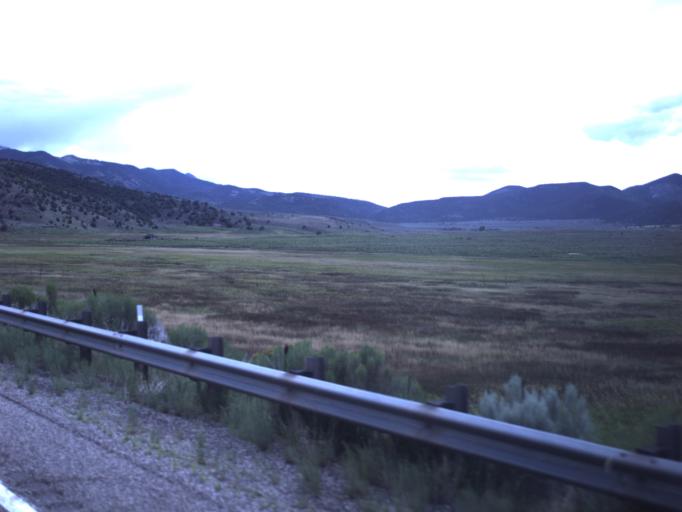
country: US
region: Utah
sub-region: Garfield County
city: Panguitch
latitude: 38.0033
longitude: -112.5094
